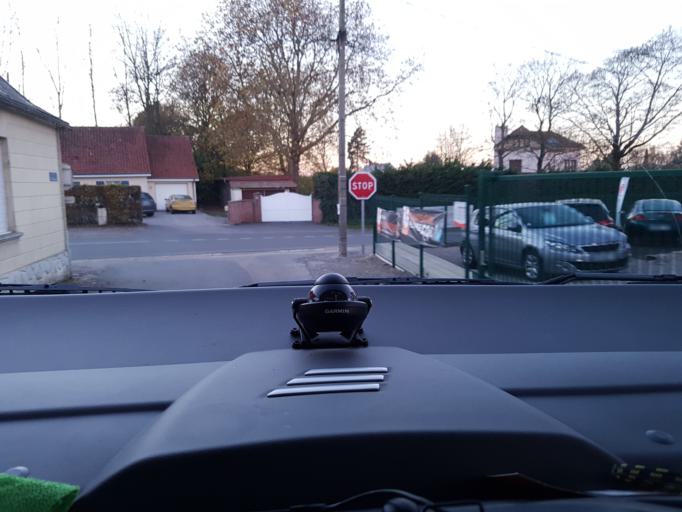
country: FR
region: Picardie
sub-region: Departement de la Somme
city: Rue
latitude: 50.3113
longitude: 1.7511
